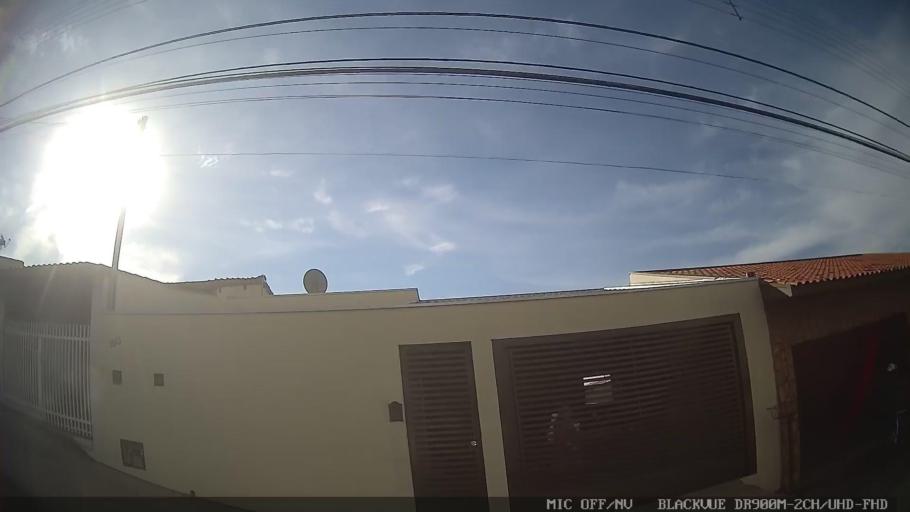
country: BR
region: Sao Paulo
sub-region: Tiete
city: Tiete
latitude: -23.0915
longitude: -47.6984
